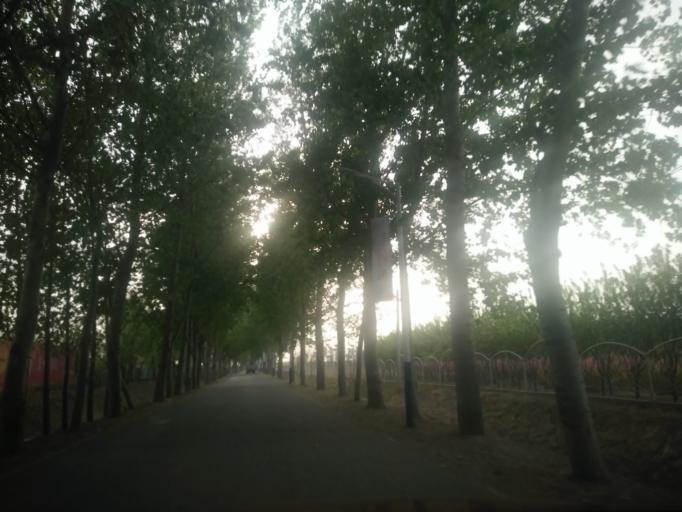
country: CN
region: Beijing
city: Weishanzhuang
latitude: 39.6753
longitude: 116.4381
